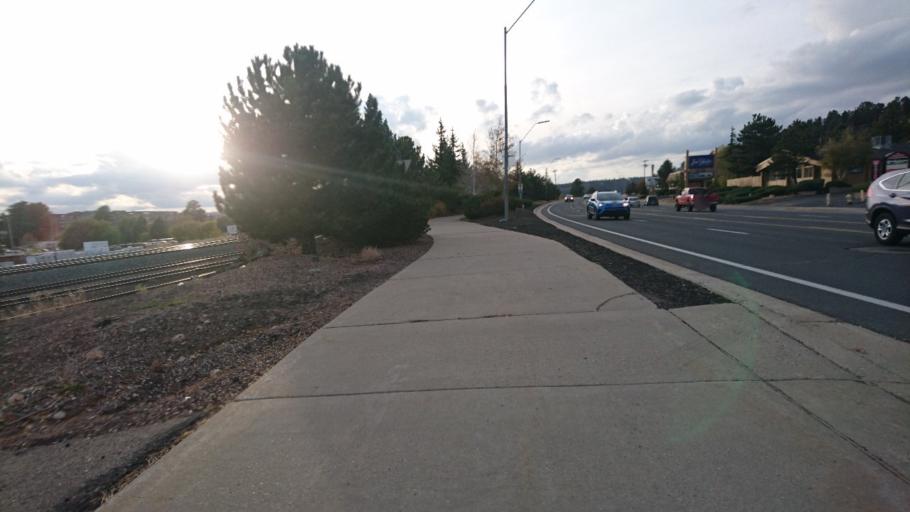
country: US
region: Arizona
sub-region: Coconino County
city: Flagstaff
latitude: 35.1936
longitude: -111.6363
